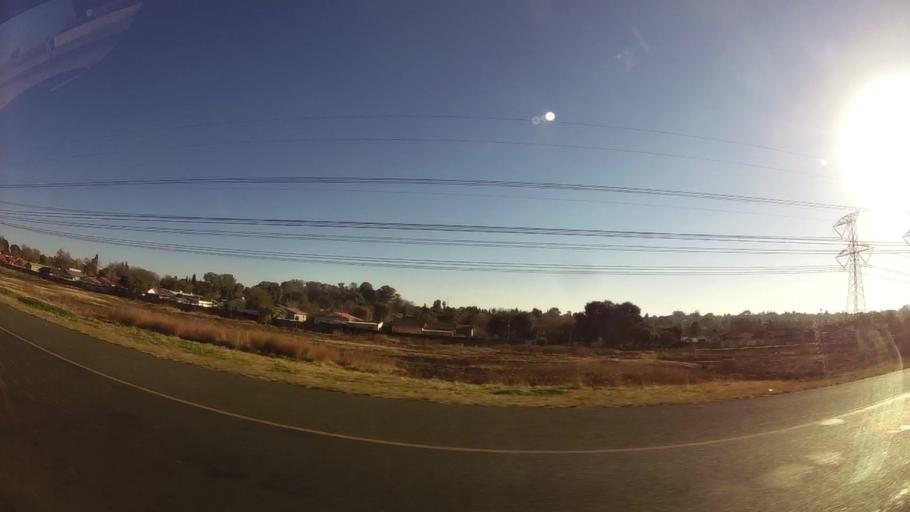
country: ZA
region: Gauteng
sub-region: City of Johannesburg Metropolitan Municipality
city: Modderfontein
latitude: -26.0882
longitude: 28.1982
